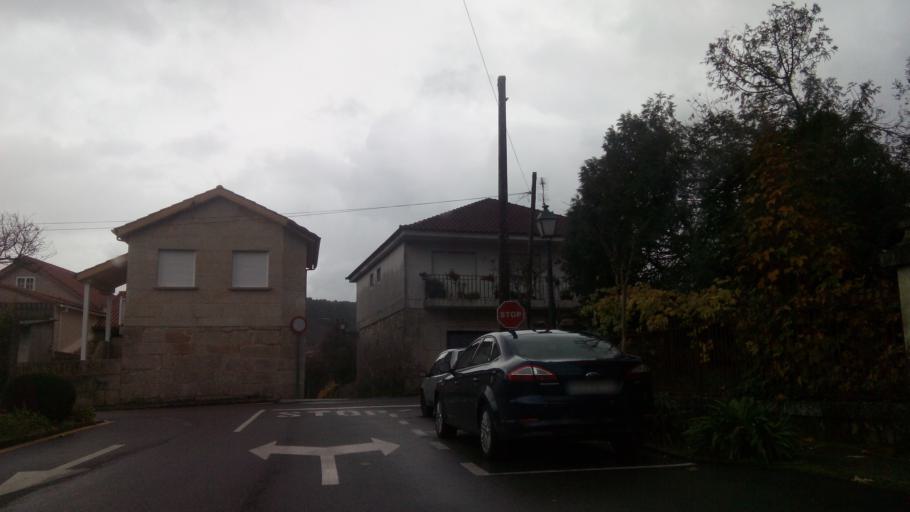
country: ES
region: Galicia
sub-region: Provincia de Pontevedra
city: Mondariz-Balneario
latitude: 42.2252
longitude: -8.4692
